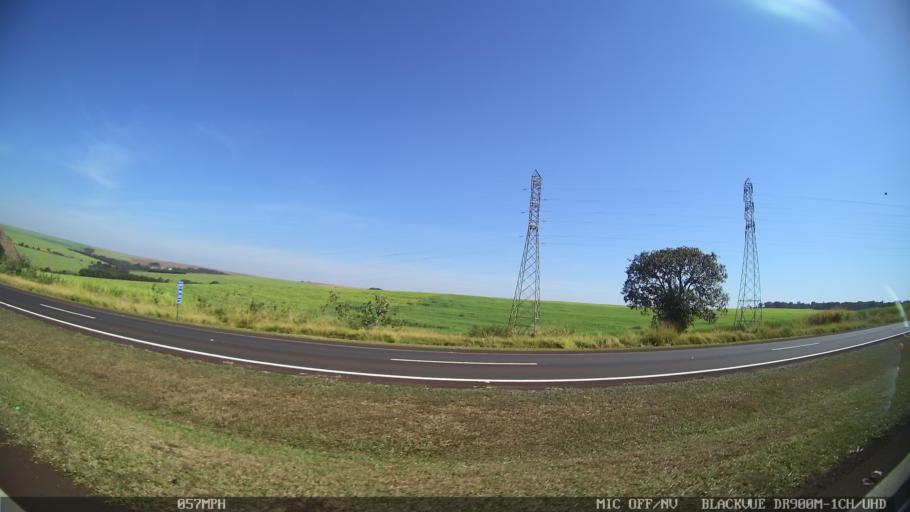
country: BR
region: Sao Paulo
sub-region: Ribeirao Preto
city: Ribeirao Preto
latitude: -21.1892
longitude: -47.8872
